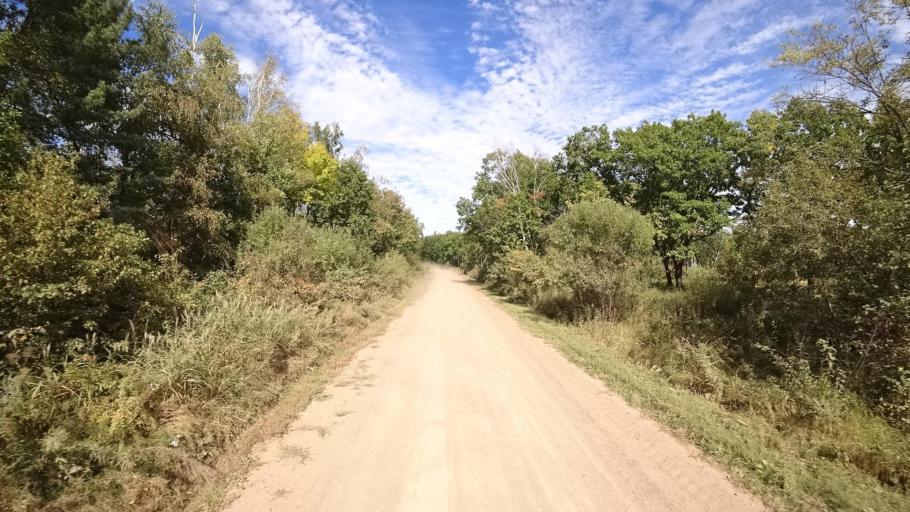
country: RU
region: Primorskiy
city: Yakovlevka
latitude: 44.3916
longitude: 133.5494
